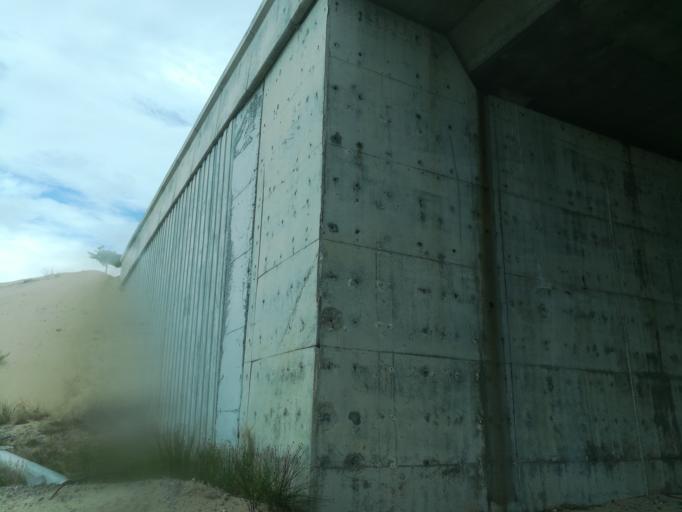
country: NG
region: Lagos
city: Ikoyi
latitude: 6.4142
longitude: 3.4180
